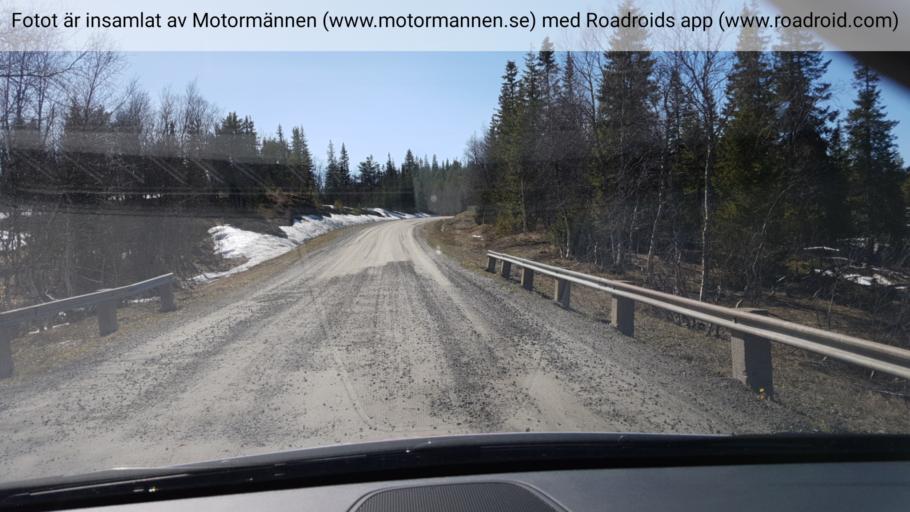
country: NO
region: Nord-Trondelag
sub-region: Snasa
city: Snaase
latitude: 63.7128
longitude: 12.4618
